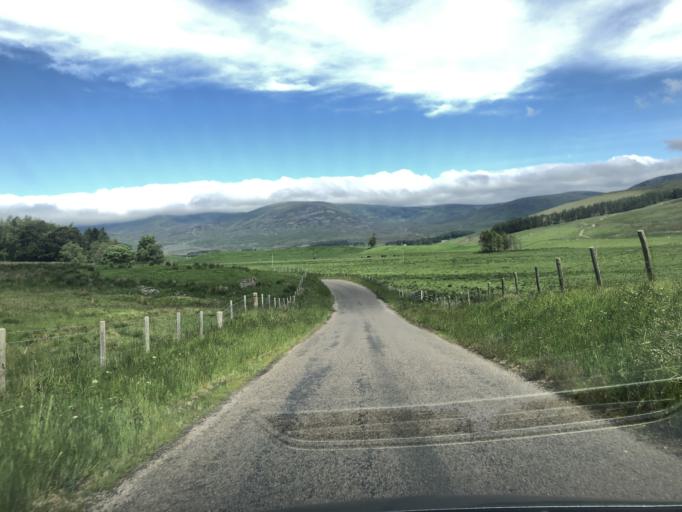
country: GB
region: Scotland
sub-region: Angus
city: Kirriemuir
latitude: 56.7911
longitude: -3.0445
